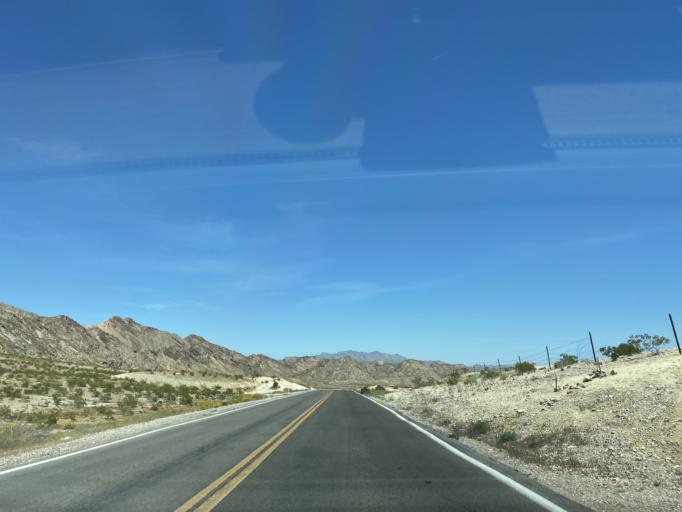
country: US
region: Nevada
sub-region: Clark County
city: Nellis Air Force Base
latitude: 36.2024
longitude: -114.9743
